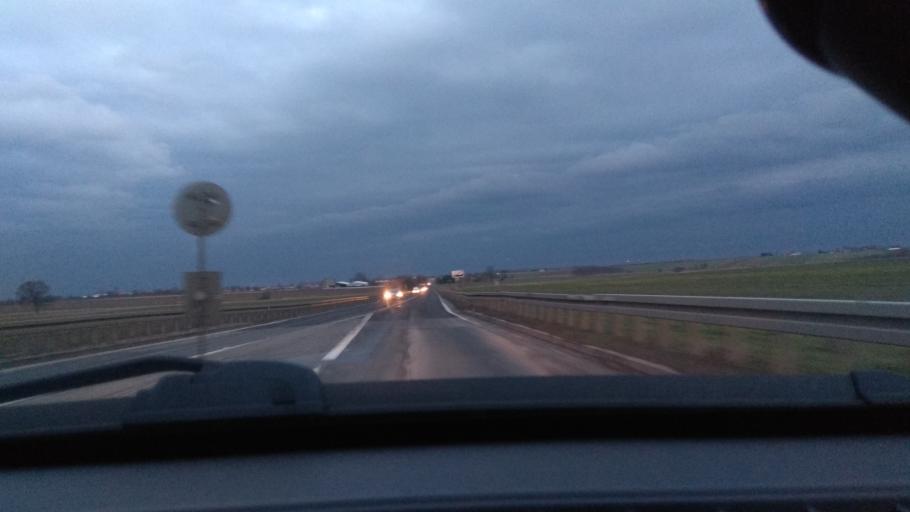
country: PL
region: Greater Poland Voivodeship
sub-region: Powiat kepinski
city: Slupia pod Kepnem
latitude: 51.2969
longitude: 18.0561
